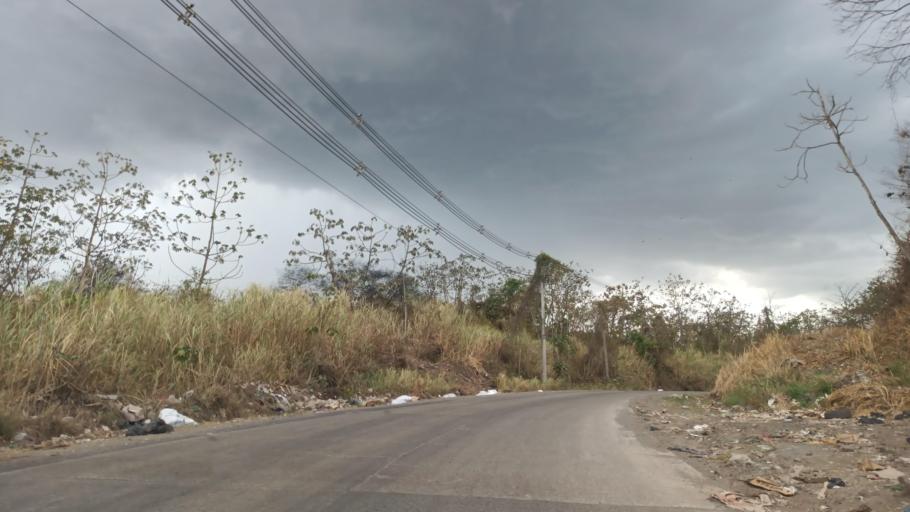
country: PA
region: Panama
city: Las Cumbres
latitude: 9.0525
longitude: -79.5622
